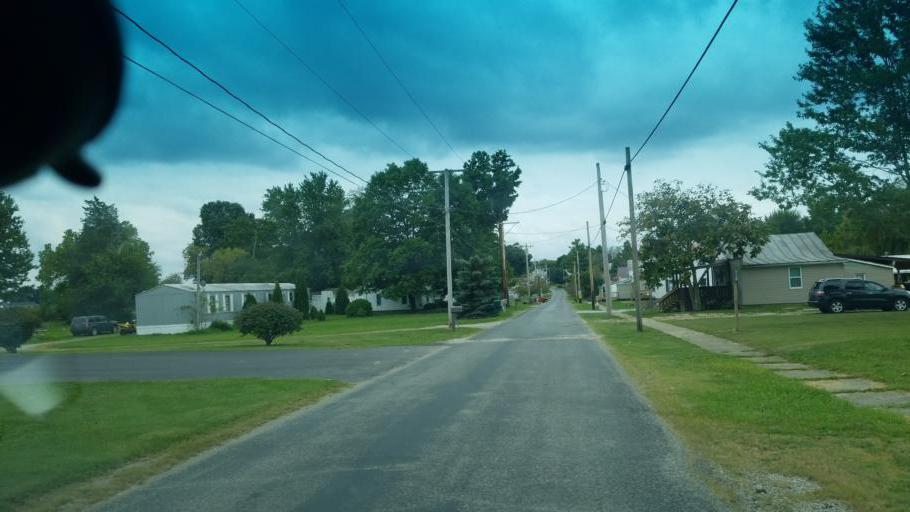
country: US
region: Ohio
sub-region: Huron County
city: Plymouth
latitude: 40.9705
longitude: -82.5973
